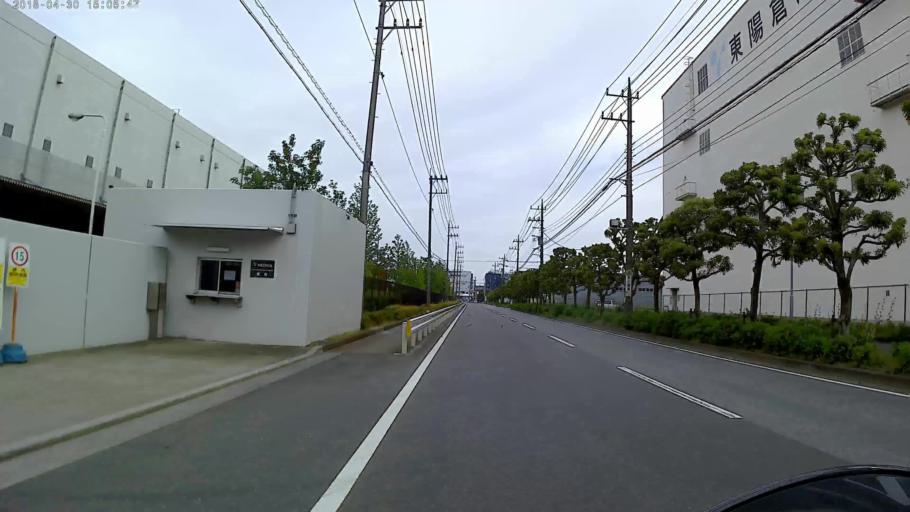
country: JP
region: Kanagawa
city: Zama
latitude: 35.5577
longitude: 139.3424
